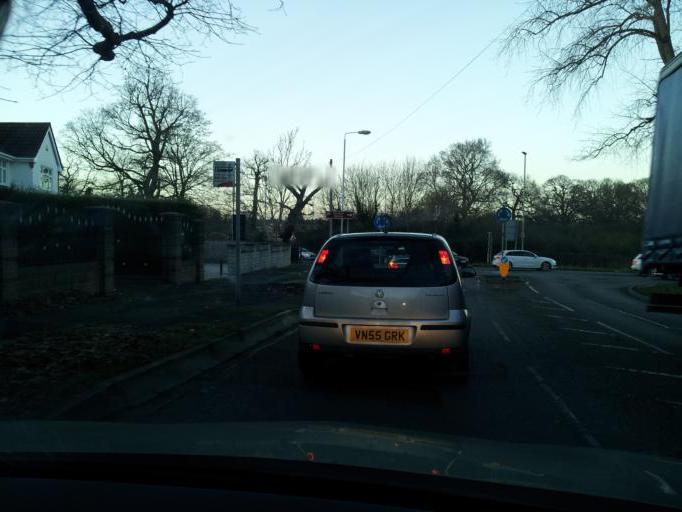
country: GB
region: England
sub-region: Leicestershire
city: Oadby
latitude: 52.6154
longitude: -1.0911
